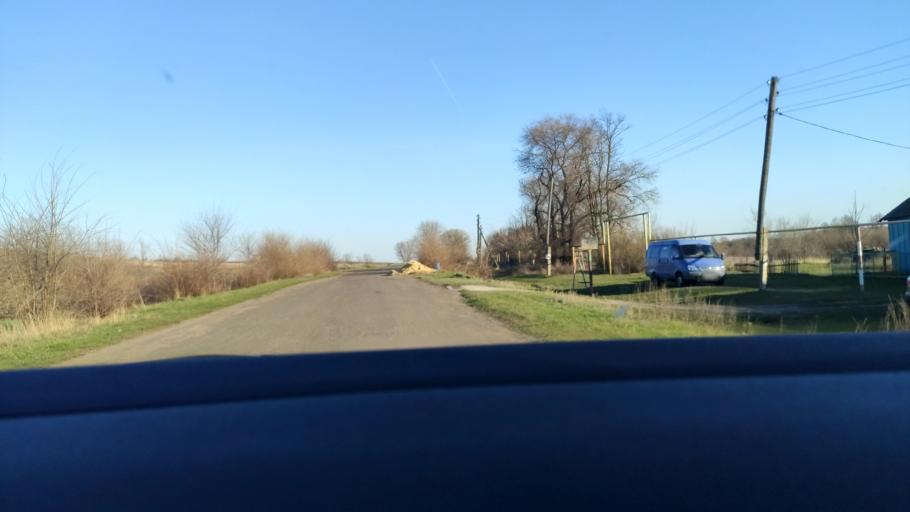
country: RU
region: Voronezj
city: Uryv-Pokrovka
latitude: 51.1465
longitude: 39.0319
